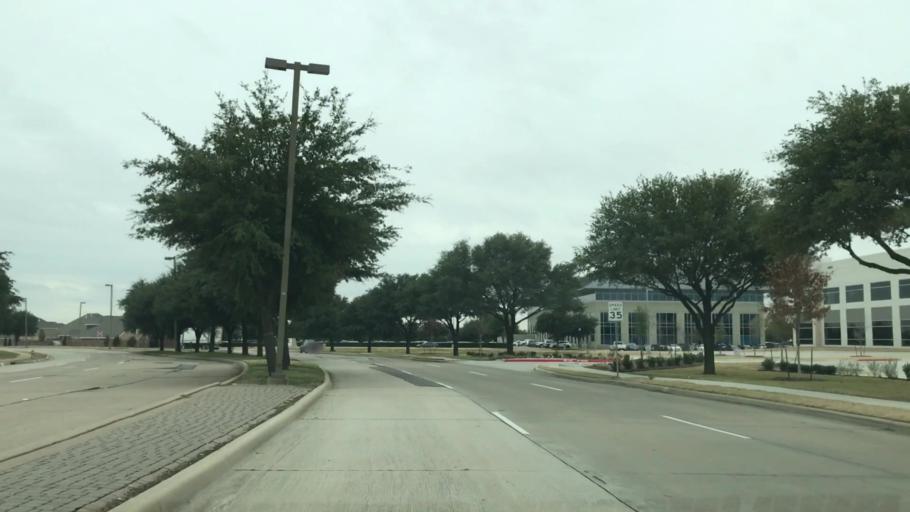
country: US
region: Texas
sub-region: Dallas County
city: Coppell
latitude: 32.9148
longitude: -96.9989
